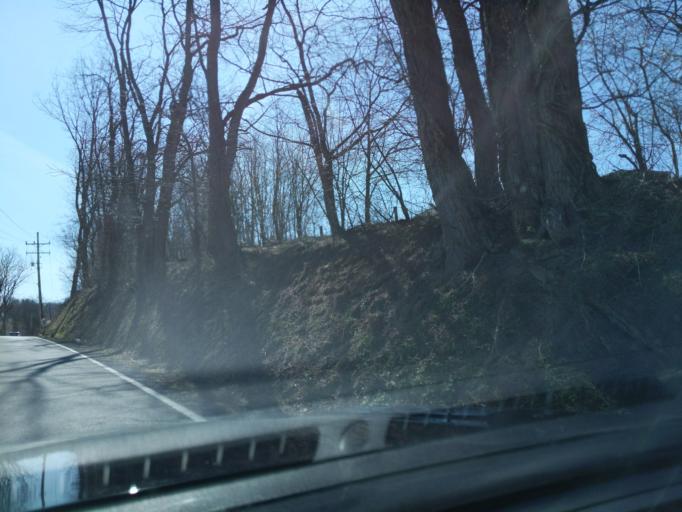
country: US
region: Pennsylvania
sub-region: Blair County
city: Duncansville
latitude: 40.4211
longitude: -78.4218
